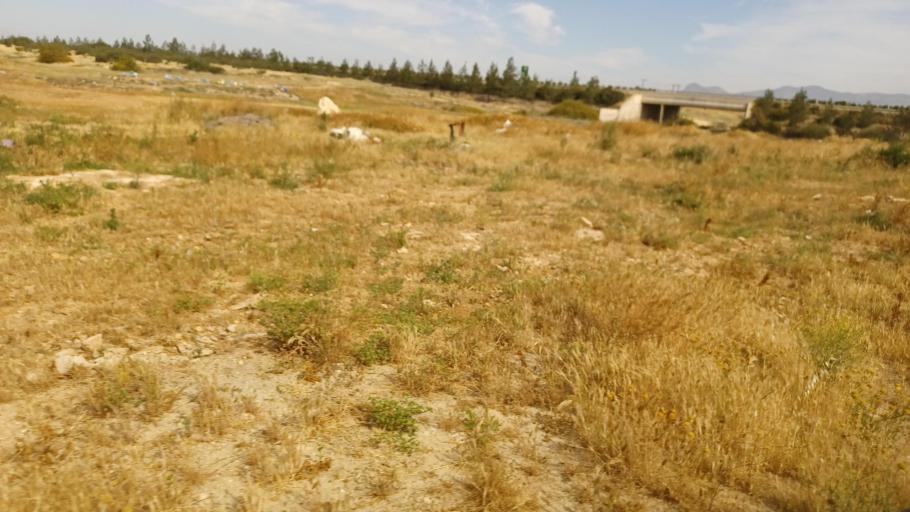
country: CY
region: Lefkosia
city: Kokkinotrimithia
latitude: 35.1596
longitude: 33.1751
